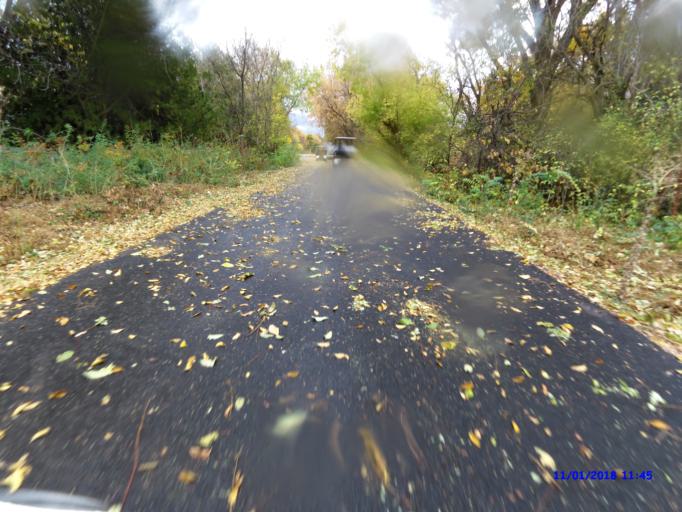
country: US
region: Utah
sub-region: Weber County
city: Ogden
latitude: 41.2361
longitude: -111.9867
